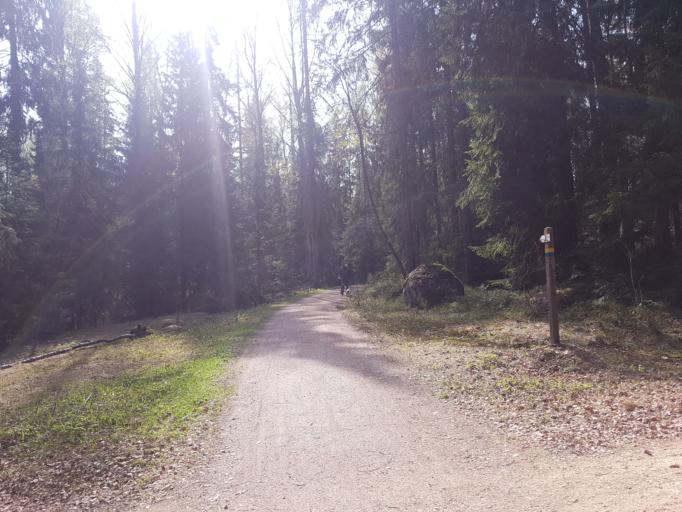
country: FI
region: Uusimaa
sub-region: Helsinki
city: Helsinki
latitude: 60.2677
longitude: 24.9249
